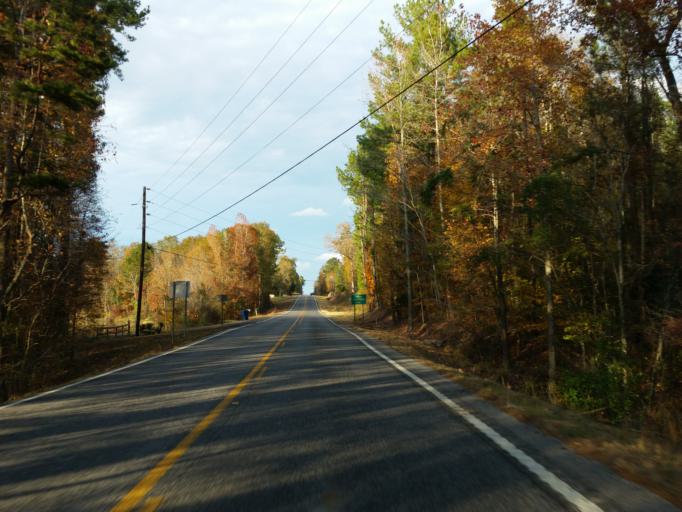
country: US
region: Mississippi
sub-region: Clarke County
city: Stonewall
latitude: 32.2244
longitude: -88.7730
